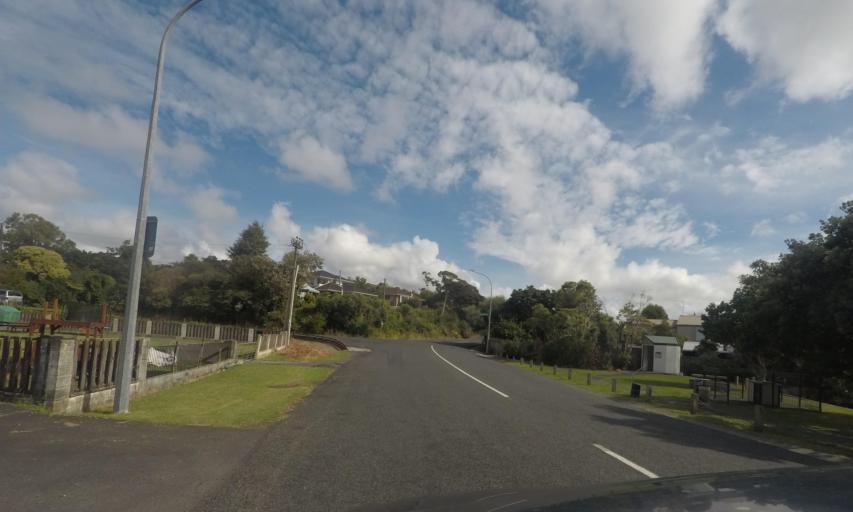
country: NZ
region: Auckland
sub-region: Auckland
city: North Shore
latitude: -36.7775
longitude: 174.6588
